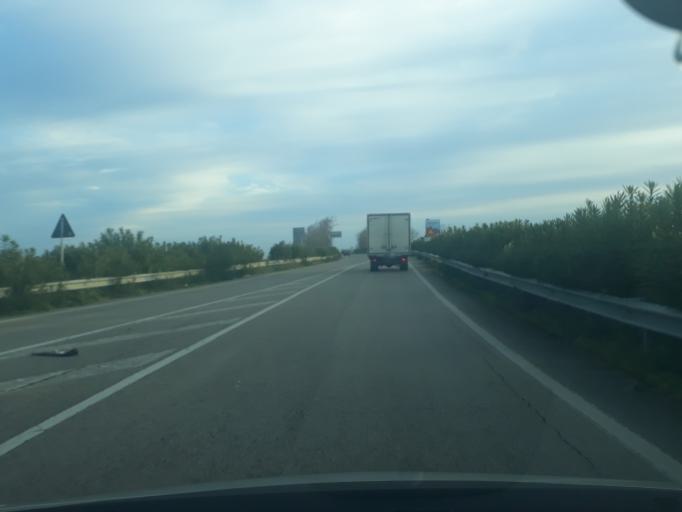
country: IT
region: Apulia
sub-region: Provincia di Brindisi
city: Brindisi
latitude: 40.6560
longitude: 17.9059
